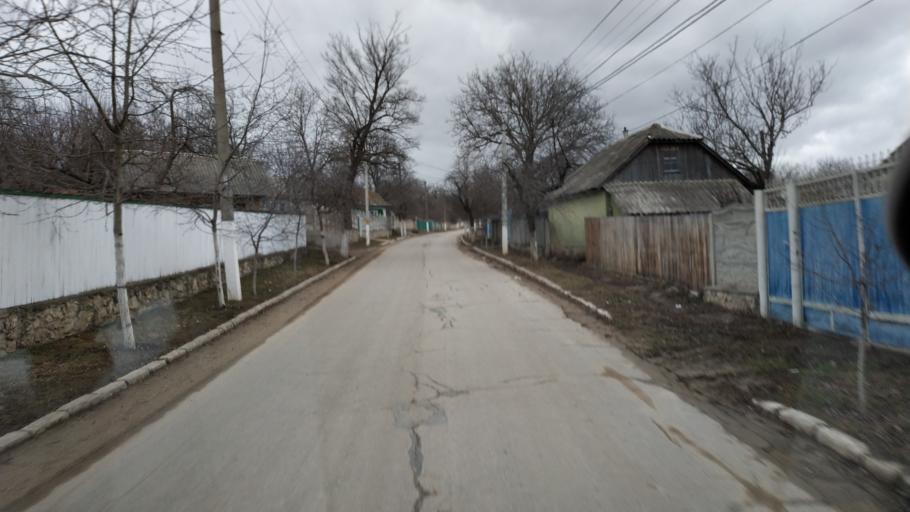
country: MD
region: Calarasi
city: Calarasi
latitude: 47.2588
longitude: 28.1383
